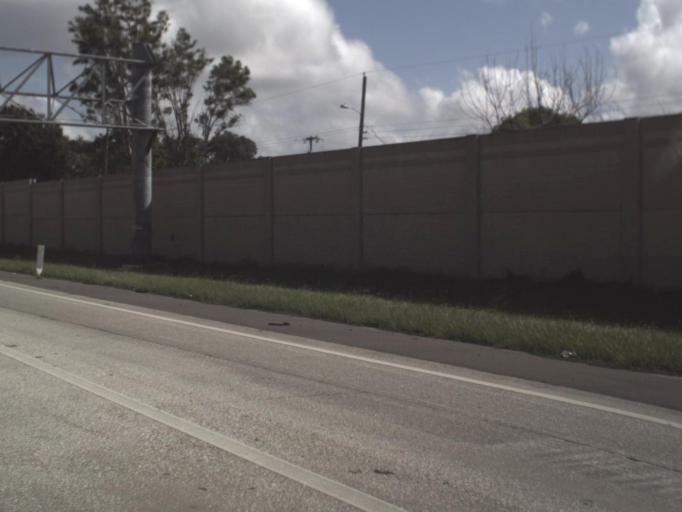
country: US
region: Florida
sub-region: Hillsborough County
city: University
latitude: 28.0494
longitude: -82.4548
